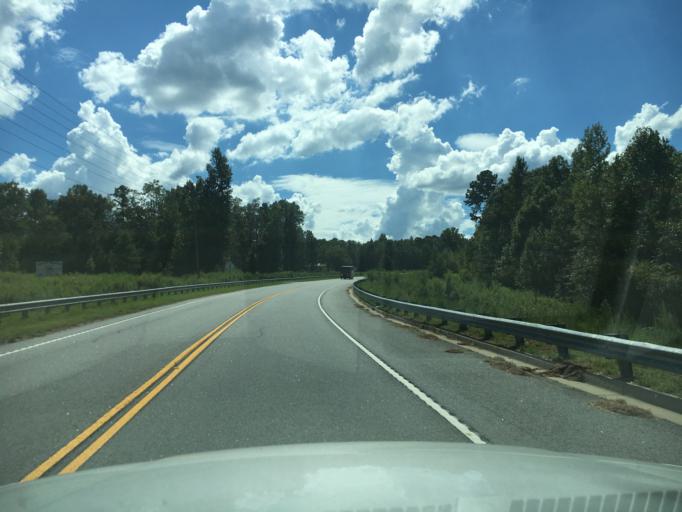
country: US
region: South Carolina
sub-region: Laurens County
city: Laurens
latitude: 34.5238
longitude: -82.1393
